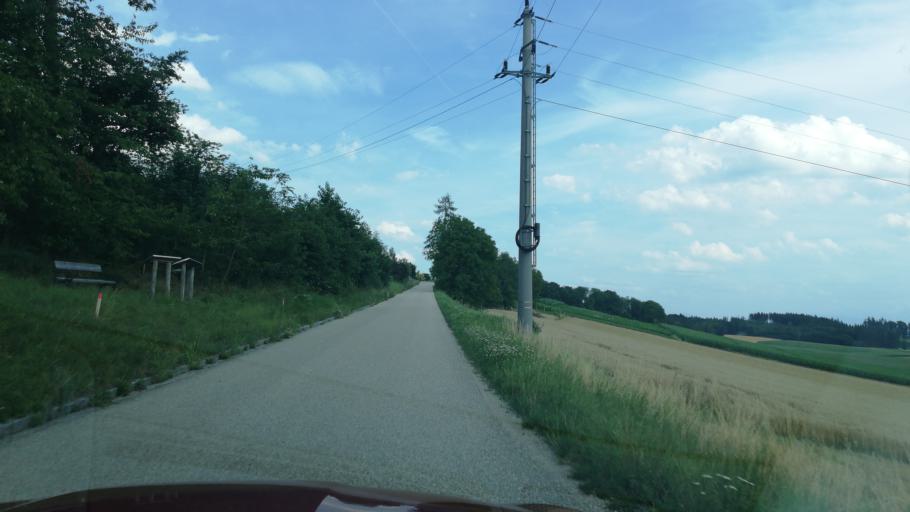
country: AT
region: Upper Austria
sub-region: Wels-Land
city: Neukirchen bei Lambach
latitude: 48.1093
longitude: 13.8228
